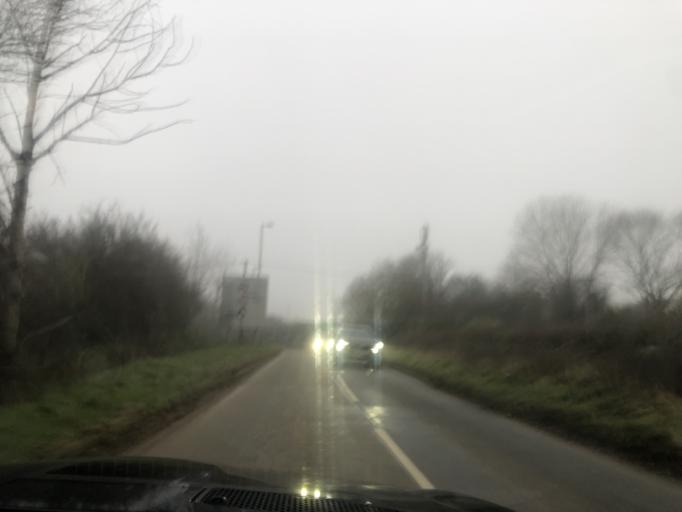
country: GB
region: England
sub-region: Oxfordshire
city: Bicester
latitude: 51.9119
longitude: -1.1710
